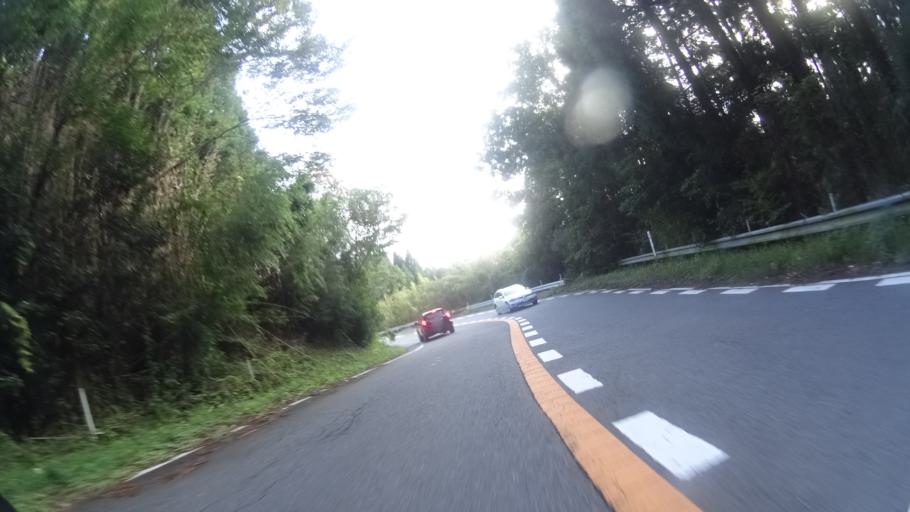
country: JP
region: Oita
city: Beppu
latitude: 33.2697
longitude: 131.4305
